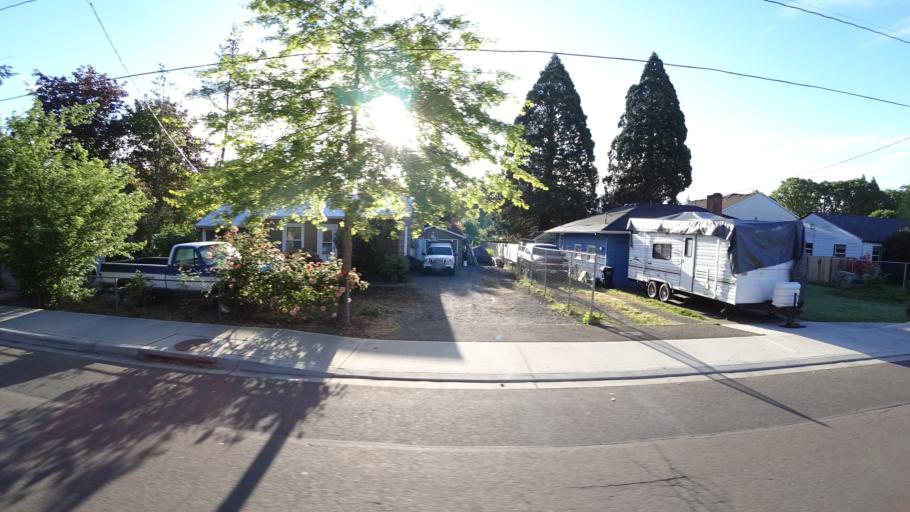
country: US
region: Oregon
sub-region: Washington County
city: Aloha
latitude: 45.4957
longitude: -122.8605
